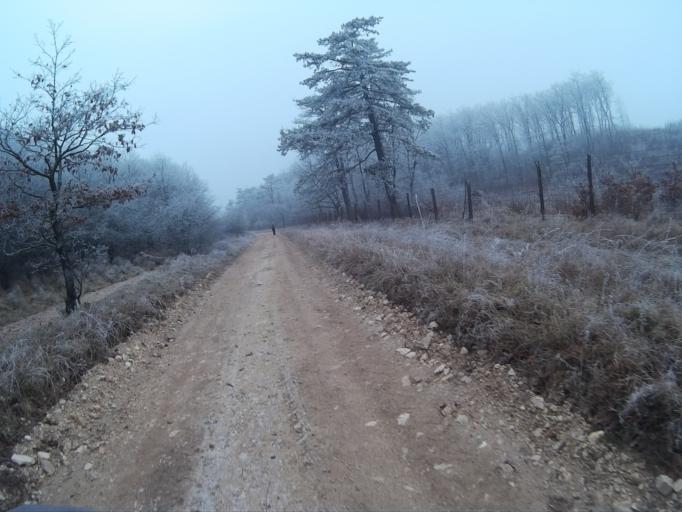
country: HU
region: Fejer
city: Zamoly
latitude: 47.3895
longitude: 18.3691
